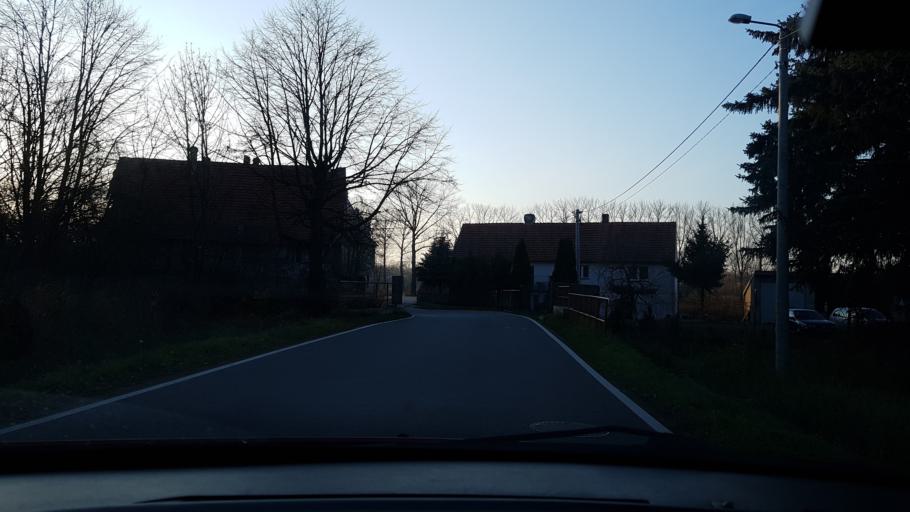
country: PL
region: Lower Silesian Voivodeship
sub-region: Powiat zabkowicki
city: Henrykow
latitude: 50.6591
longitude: 17.0253
